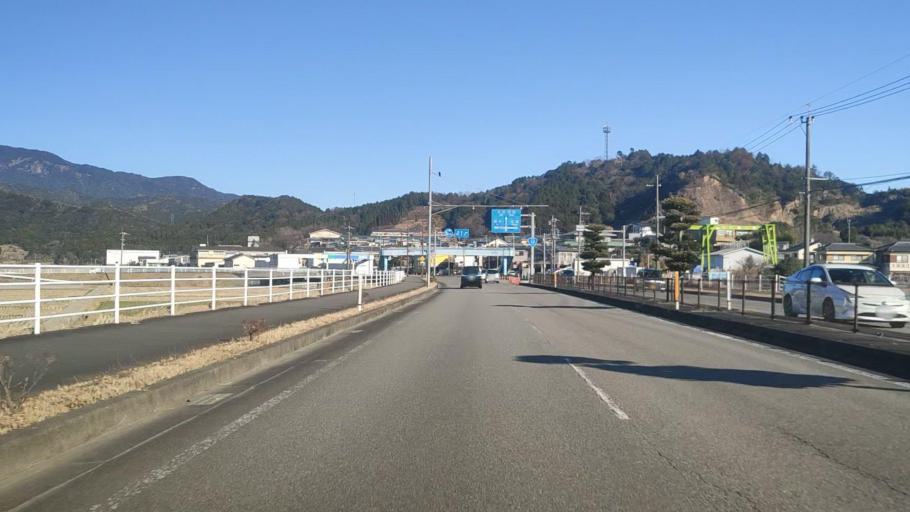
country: JP
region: Miyazaki
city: Nobeoka
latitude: 32.6081
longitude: 131.6832
